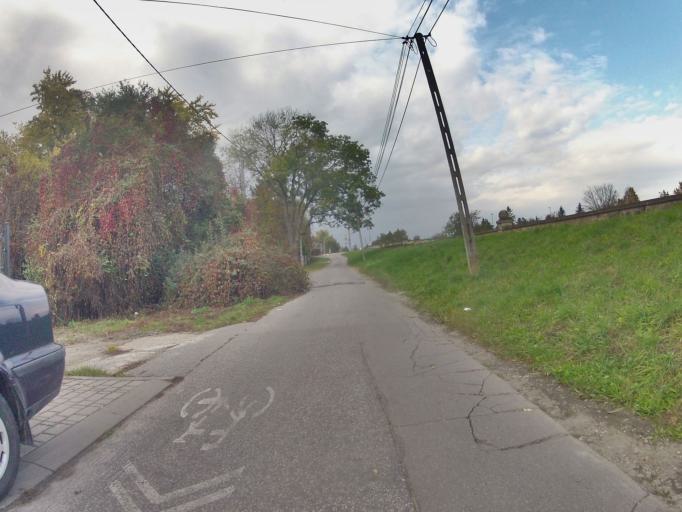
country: PL
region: Lesser Poland Voivodeship
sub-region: Krakow
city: Krakow
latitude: 50.0593
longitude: 19.9018
